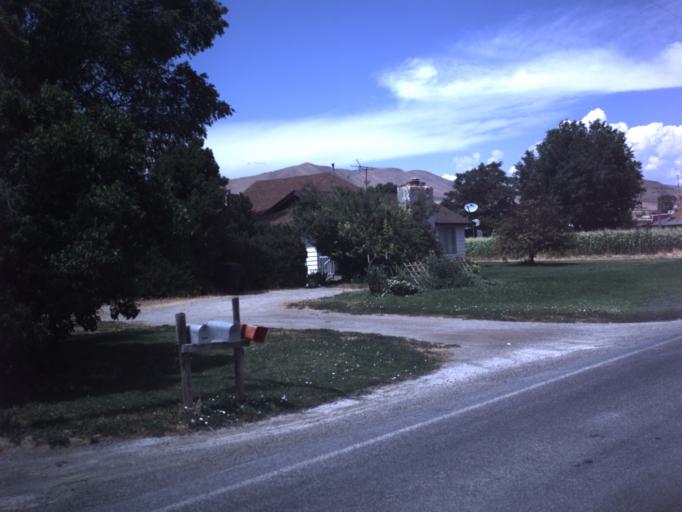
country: US
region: Utah
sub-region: Box Elder County
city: Tremonton
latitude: 41.6820
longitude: -112.2969
